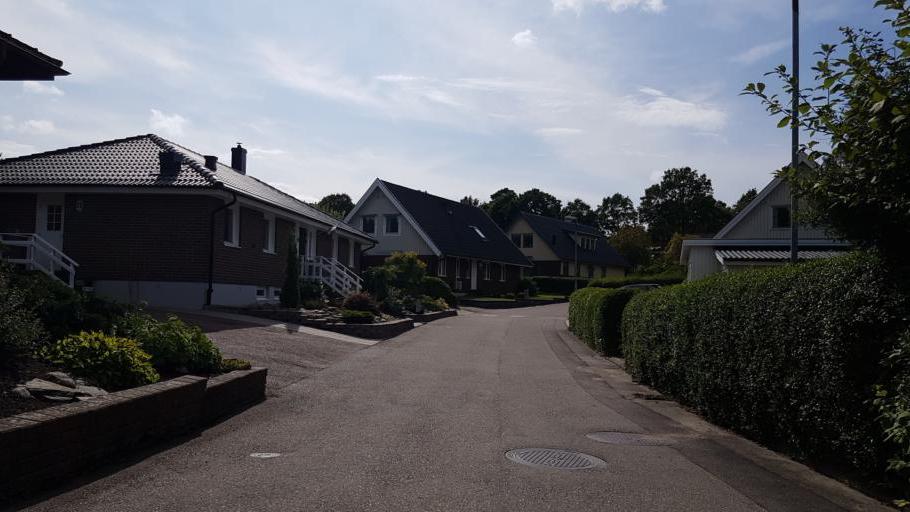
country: SE
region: Vaestra Goetaland
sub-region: Harryda Kommun
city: Molnlycke
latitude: 57.6662
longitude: 12.1078
